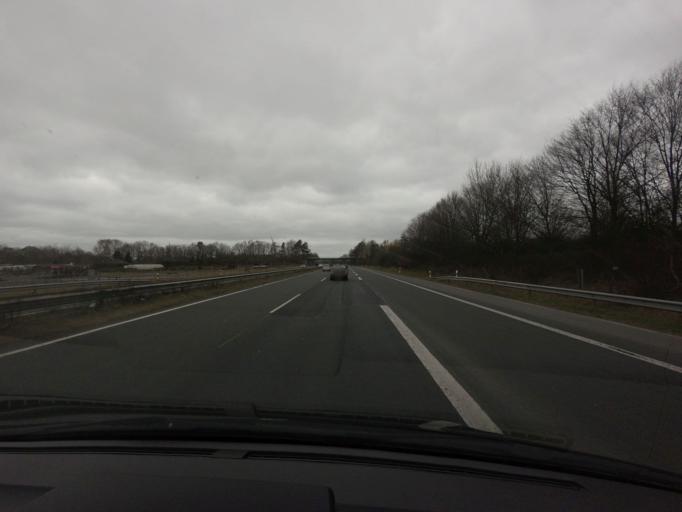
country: DE
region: Lower Saxony
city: Wiefelstede
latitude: 53.1911
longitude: 8.1017
